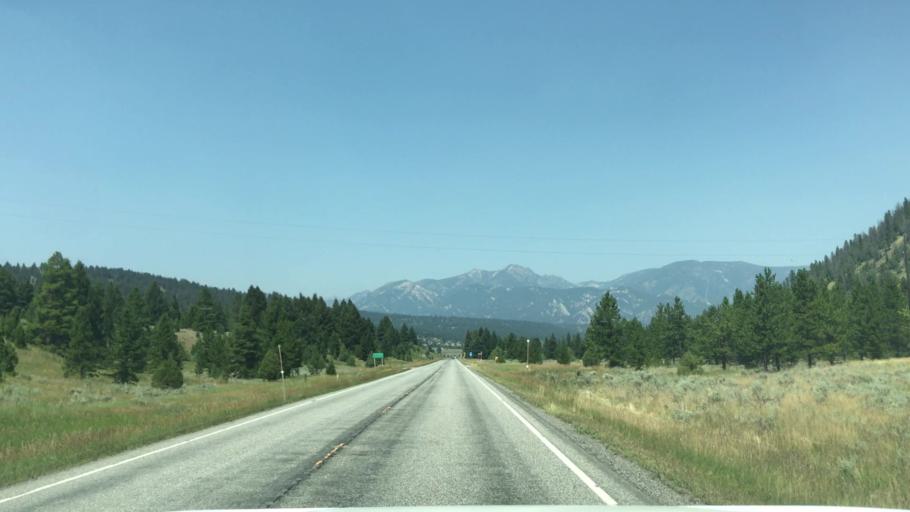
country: US
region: Montana
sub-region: Gallatin County
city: Big Sky
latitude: 45.2061
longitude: -111.2430
